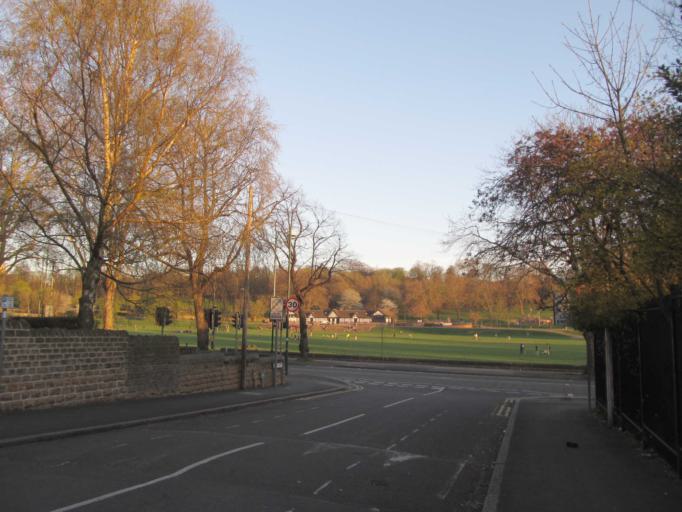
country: GB
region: England
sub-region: Nottingham
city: Nottingham
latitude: 52.9672
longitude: -1.1620
